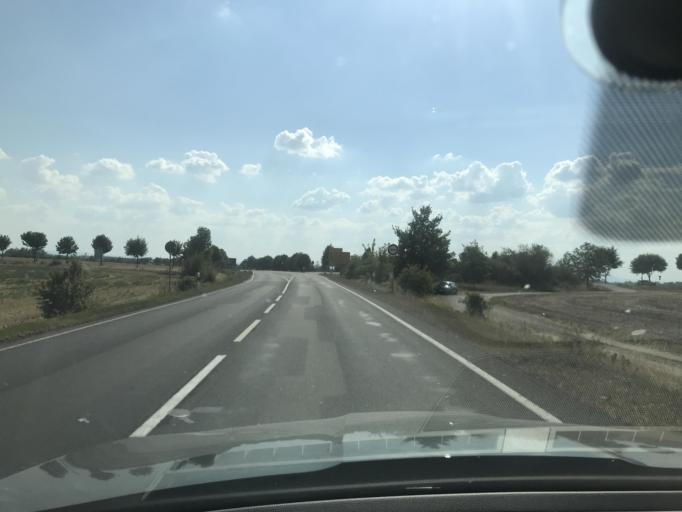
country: DE
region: Saxony-Anhalt
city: Groeningen
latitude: 51.9433
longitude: 11.1915
